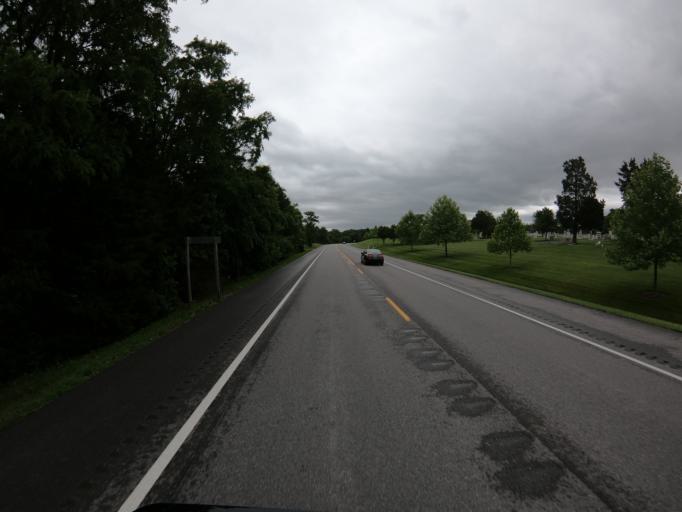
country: US
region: Maryland
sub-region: Washington County
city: Keedysville
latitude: 39.4876
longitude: -77.7030
